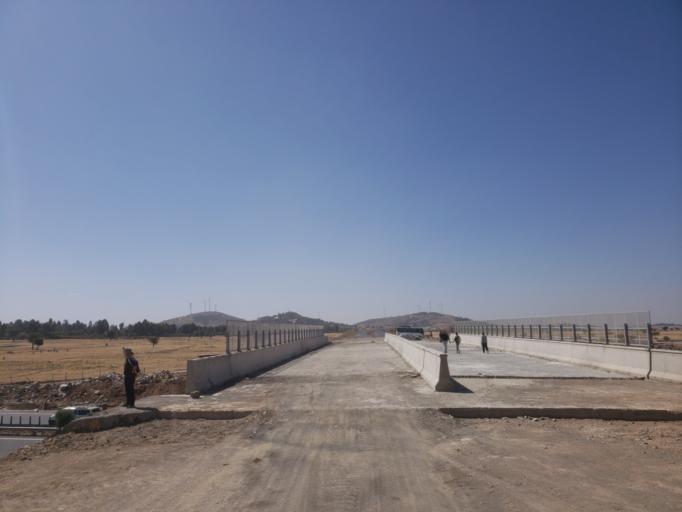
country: ET
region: Oromiya
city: Mojo
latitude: 8.5798
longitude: 39.1734
